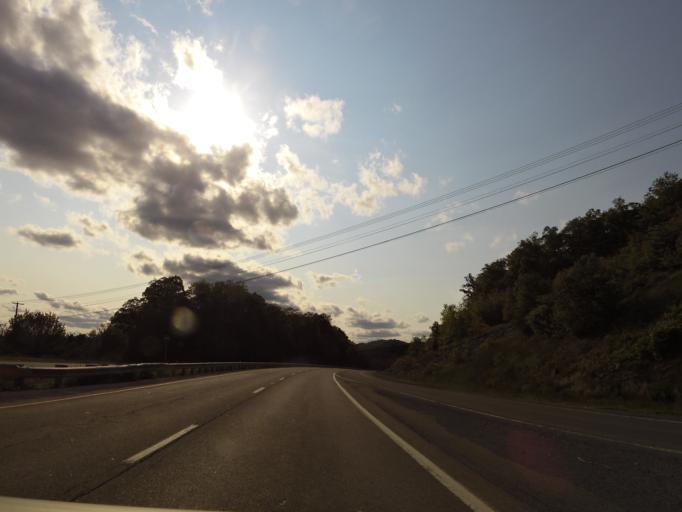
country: US
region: Virginia
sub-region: Tazewell County
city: Bluefield
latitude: 37.2385
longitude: -81.2643
